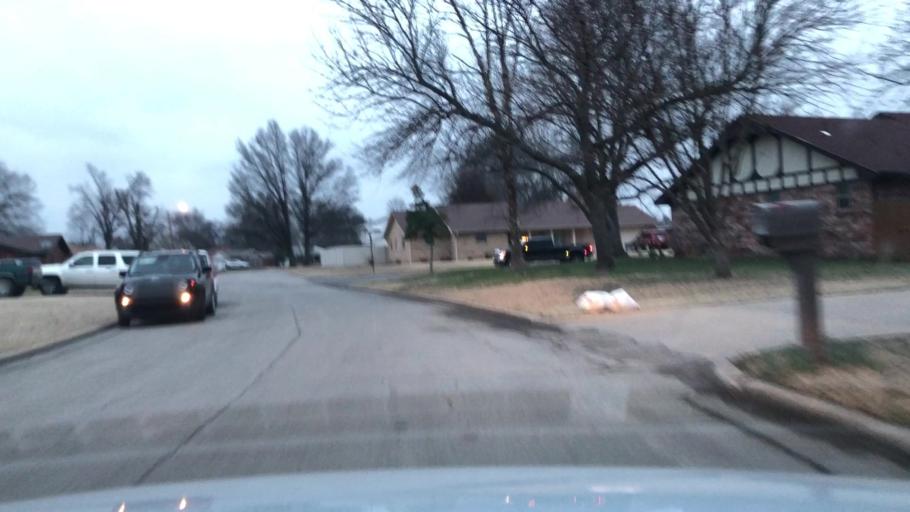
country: US
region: Oklahoma
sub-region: Washington County
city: Dewey
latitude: 36.7815
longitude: -95.9407
